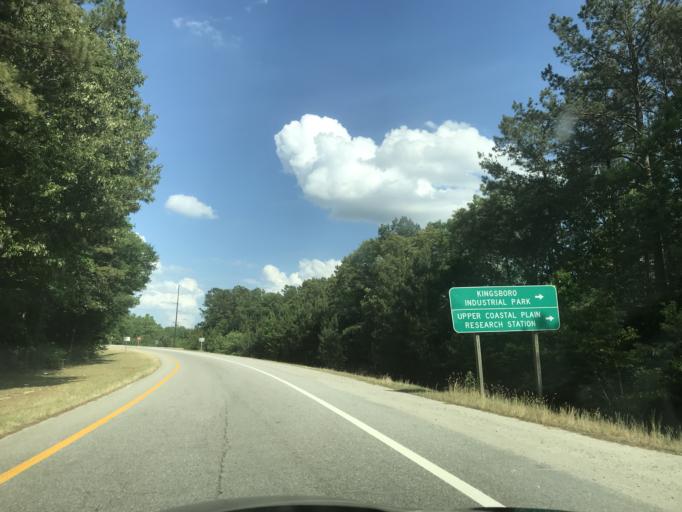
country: US
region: North Carolina
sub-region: Nash County
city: Rocky Mount
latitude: 35.9248
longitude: -77.6765
